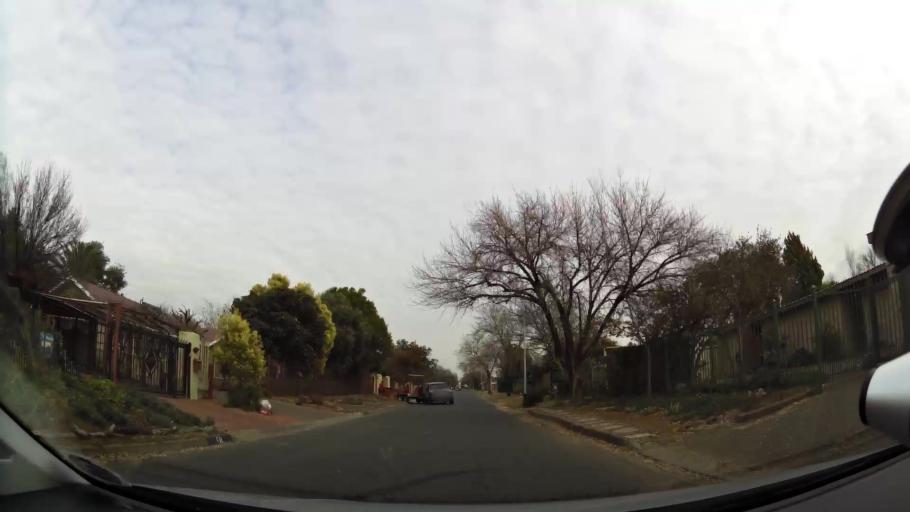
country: ZA
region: Orange Free State
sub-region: Mangaung Metropolitan Municipality
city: Bloemfontein
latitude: -29.1253
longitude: 26.1786
